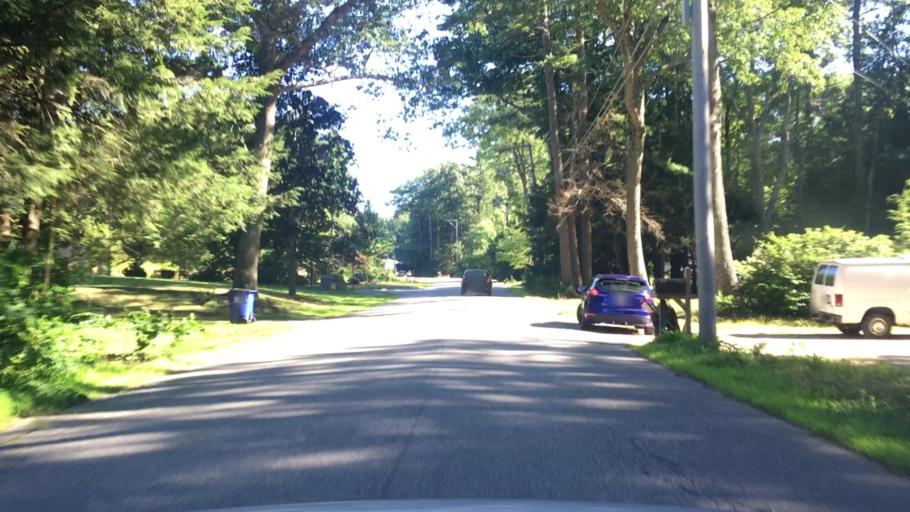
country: US
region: New Hampshire
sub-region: Rockingham County
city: Exeter
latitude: 43.0150
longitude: -70.9798
